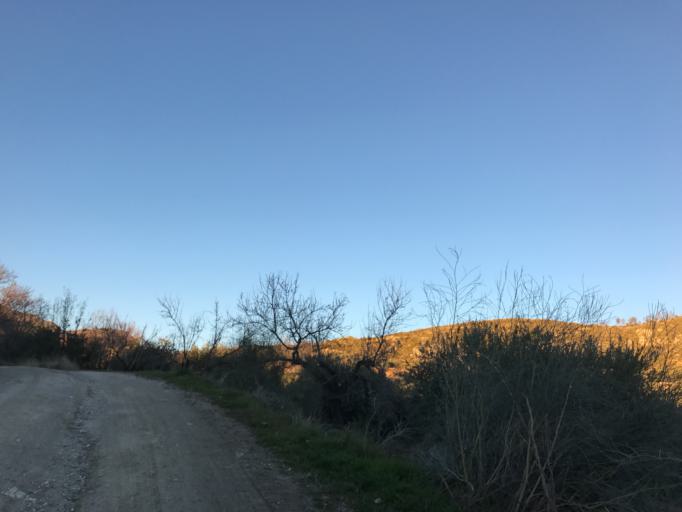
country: ES
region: Andalusia
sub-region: Provincia de Granada
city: Beas de Granada
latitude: 37.2232
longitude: -3.4727
